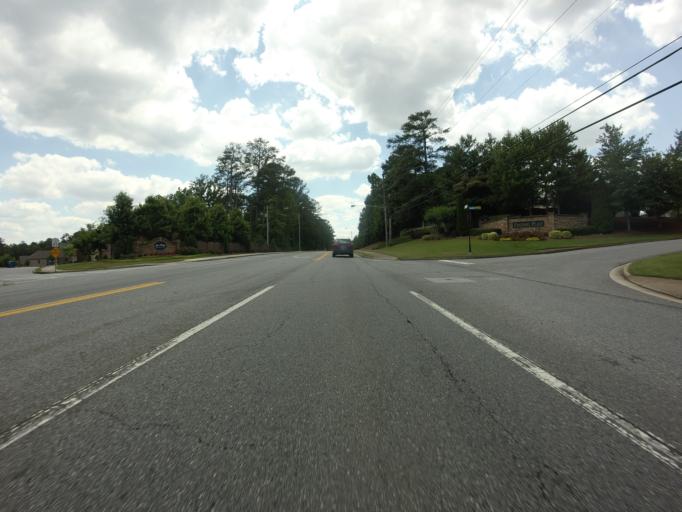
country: US
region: Georgia
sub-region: Fulton County
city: Johns Creek
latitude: 34.0396
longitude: -84.2307
